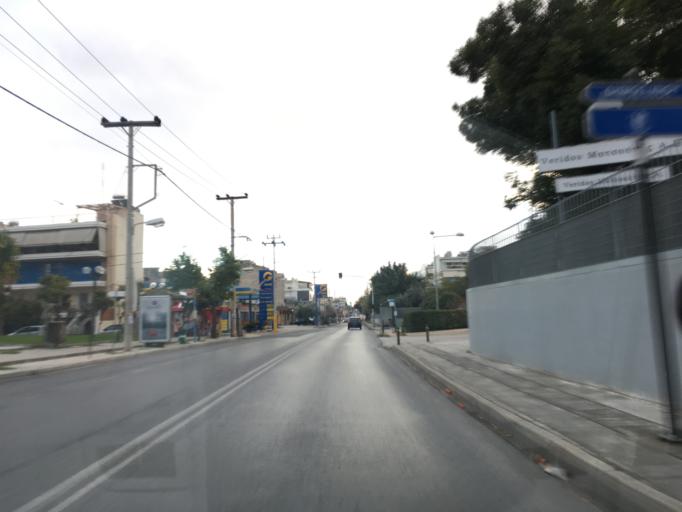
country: GR
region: Attica
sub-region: Nomarchia Athinas
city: Nea Filadelfeia
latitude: 38.0458
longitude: 23.7287
